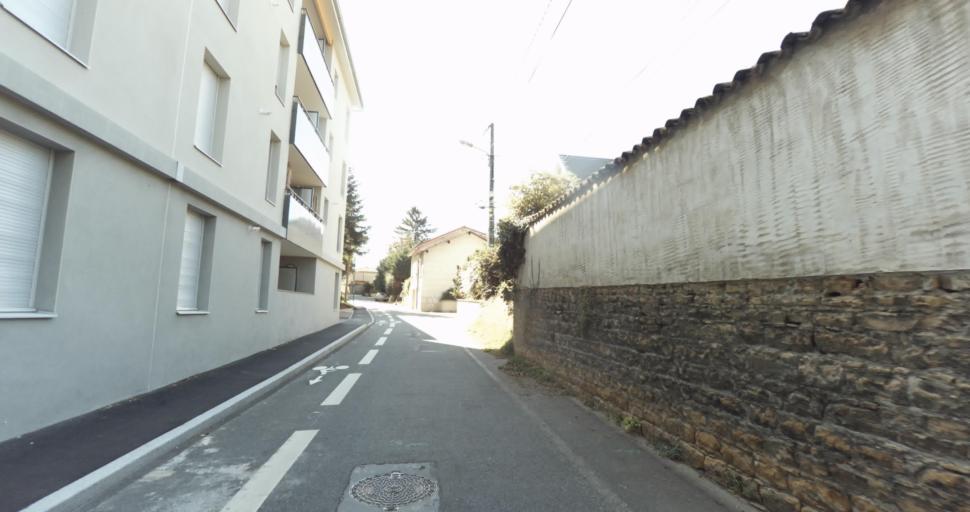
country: FR
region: Rhone-Alpes
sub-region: Departement du Rhone
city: Neuville-sur-Saone
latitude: 45.8750
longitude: 4.8438
